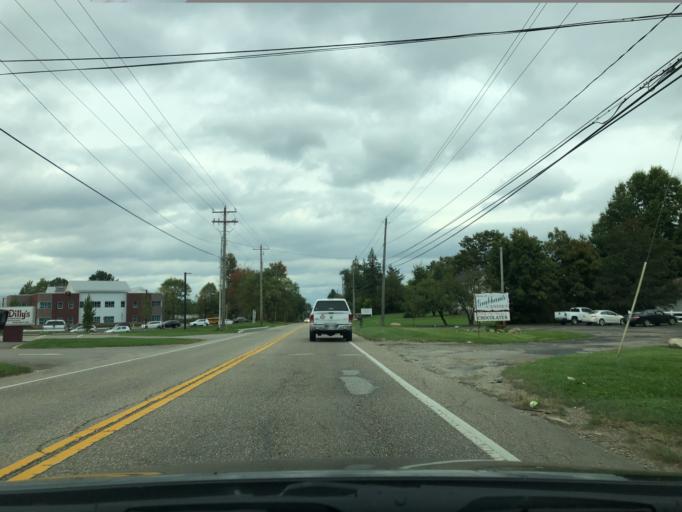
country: US
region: Ohio
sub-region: Summit County
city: Cuyahoga Falls
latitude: 41.1876
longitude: -81.5077
